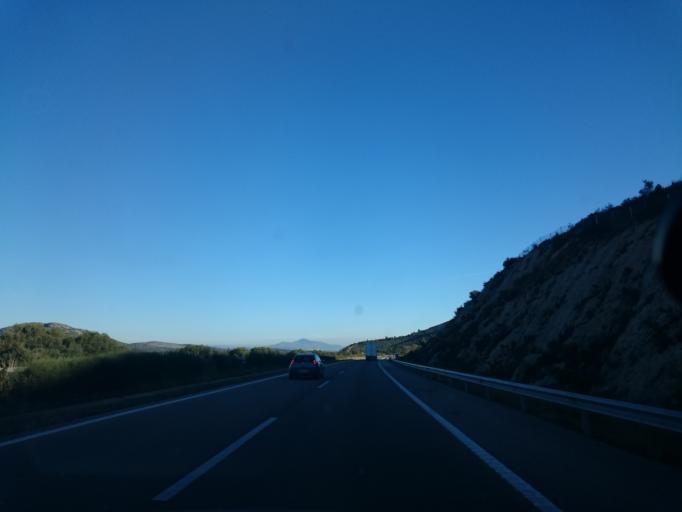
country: ES
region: Valencia
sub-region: Provincia de Castello
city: Santa Magdalena de Pulpis
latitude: 40.3735
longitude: 0.3341
